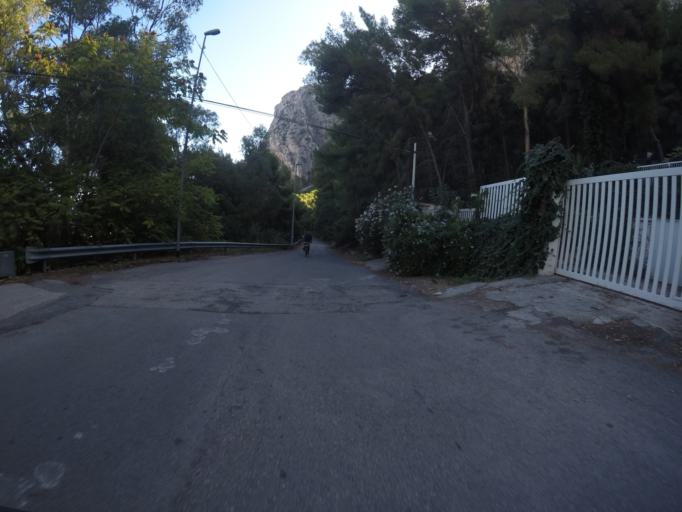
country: IT
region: Sicily
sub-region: Palermo
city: Palermo
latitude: 38.1869
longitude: 13.3459
